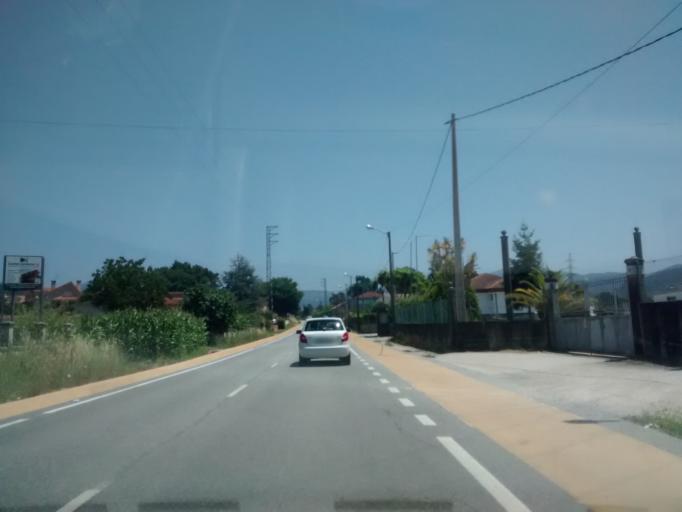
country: ES
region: Galicia
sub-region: Provincia de Pontevedra
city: Nigran
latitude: 42.1141
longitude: -8.7959
